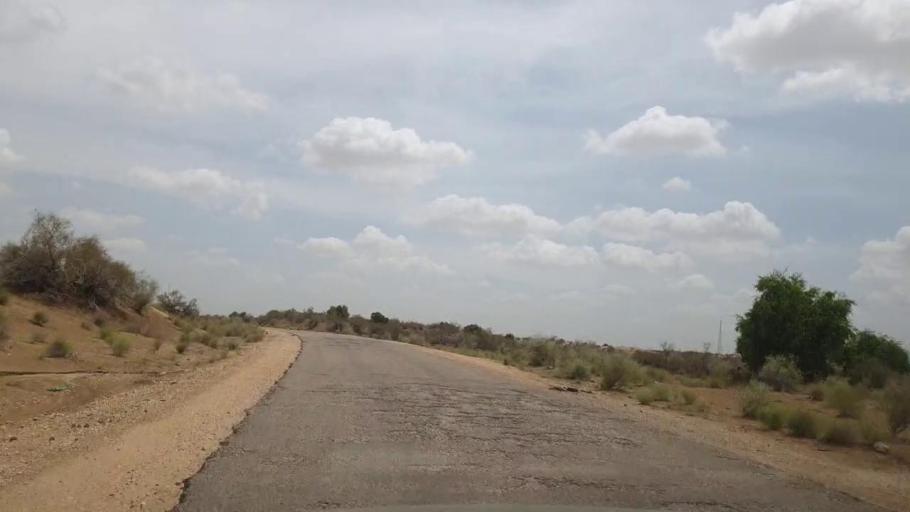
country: PK
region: Sindh
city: Kot Diji
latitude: 27.1442
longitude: 69.2246
